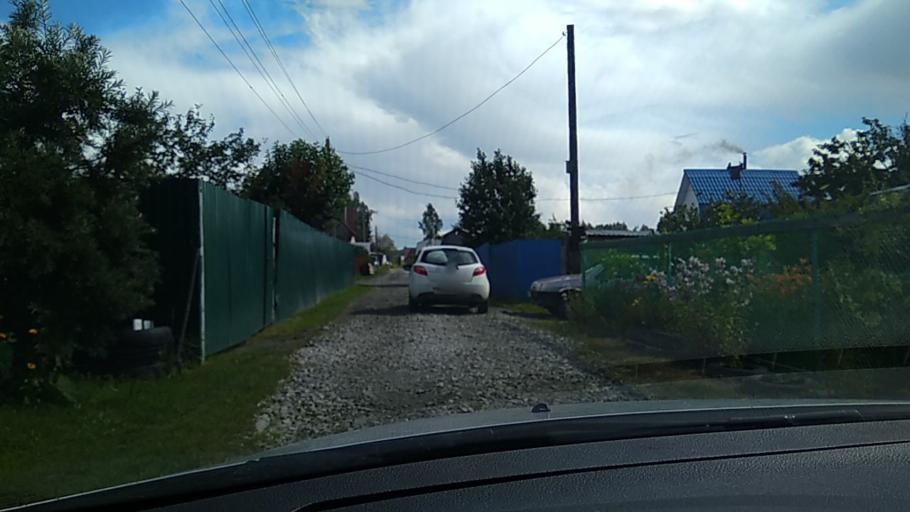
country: RU
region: Sverdlovsk
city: Sredneuralsk
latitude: 56.9700
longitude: 60.4671
